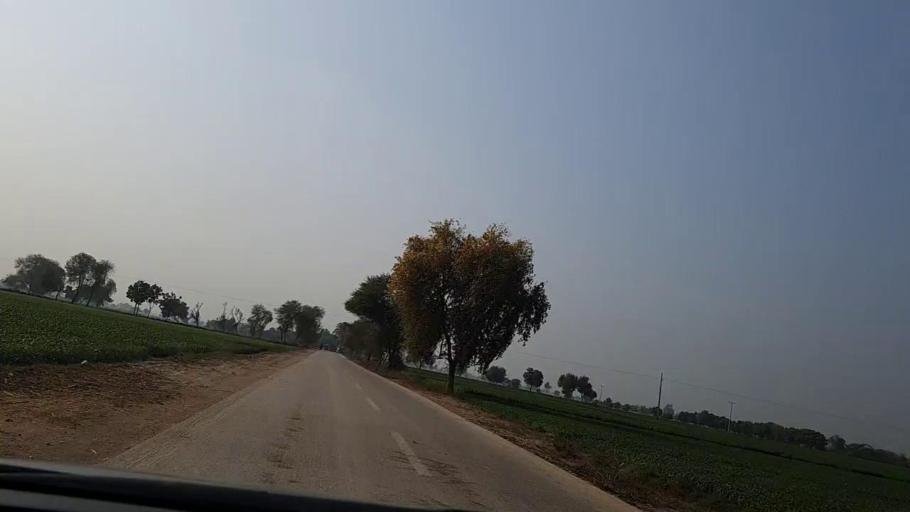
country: PK
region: Sindh
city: Sakrand
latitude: 26.1324
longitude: 68.2126
